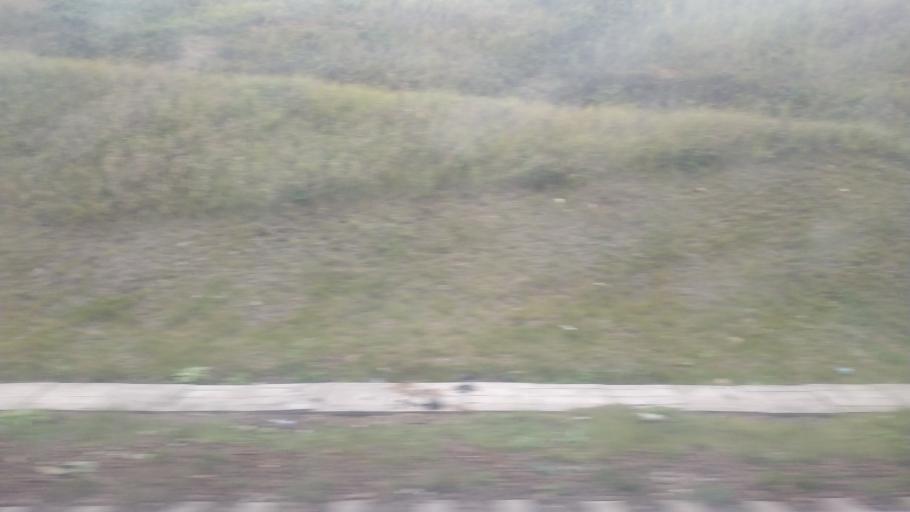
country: RU
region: Moskovskaya
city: Ozherel'ye
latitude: 54.8117
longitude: 38.2688
